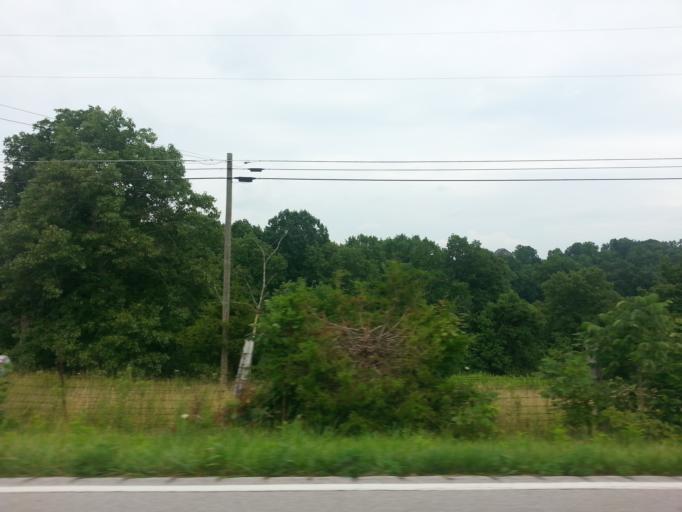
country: US
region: Kentucky
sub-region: Robertson County
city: Mount Olivet
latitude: 38.5285
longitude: -84.0600
